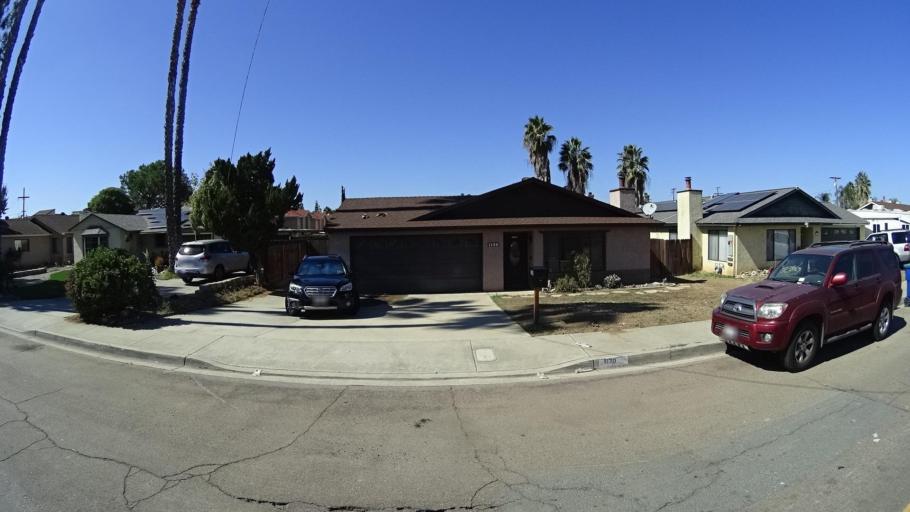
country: US
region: California
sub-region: San Diego County
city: El Cajon
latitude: 32.8109
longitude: -116.9552
